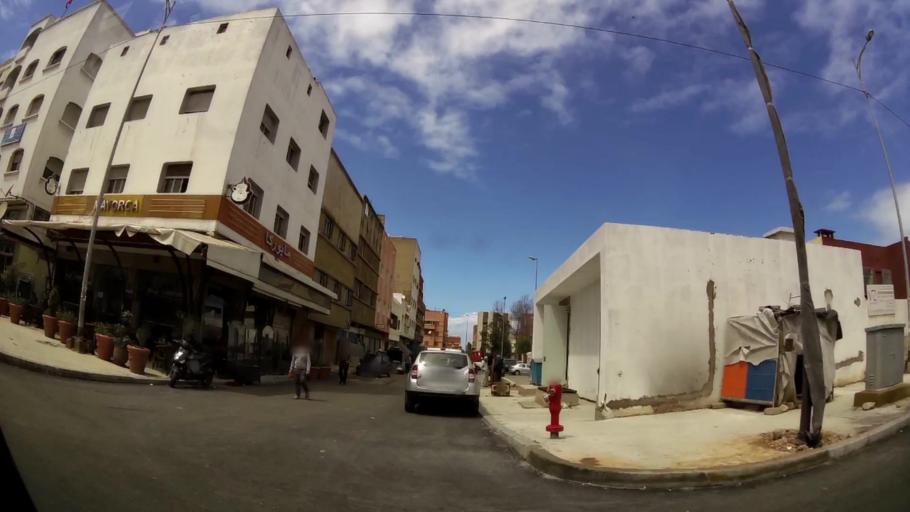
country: MA
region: Grand Casablanca
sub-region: Mediouna
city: Tit Mellil
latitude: 33.6066
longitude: -7.5183
